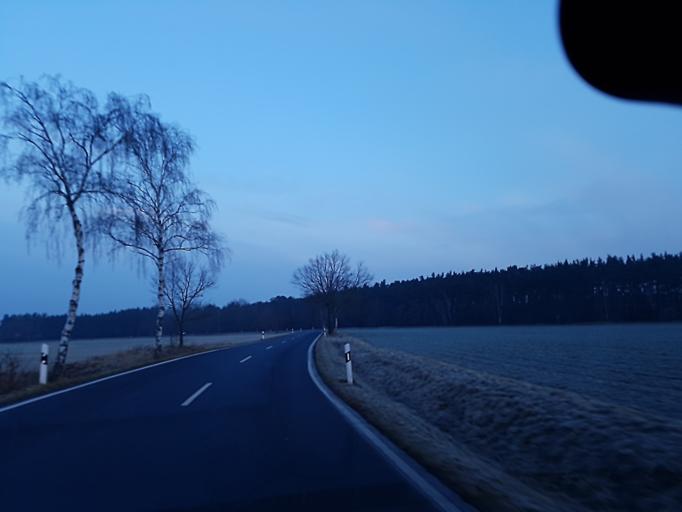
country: DE
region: Saxony-Anhalt
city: Holzdorf
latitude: 51.7535
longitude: 13.1401
